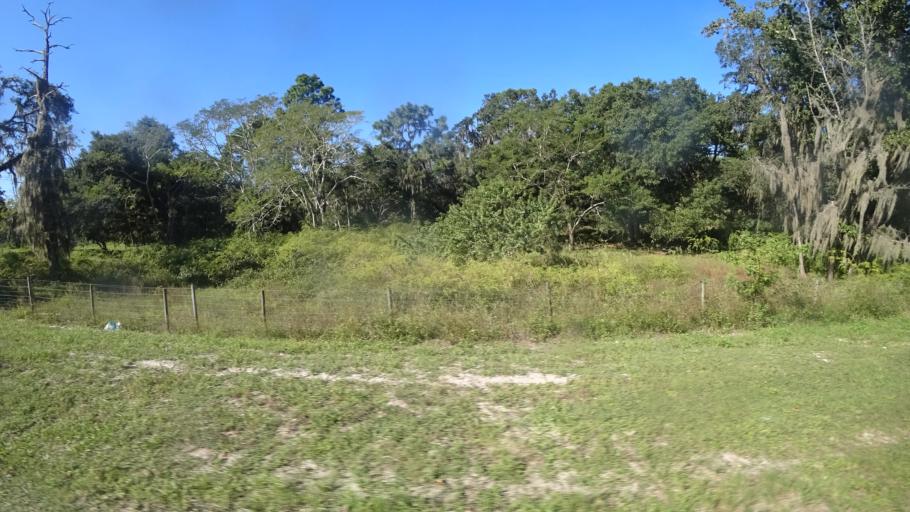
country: US
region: Florida
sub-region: Hillsborough County
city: Wimauma
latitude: 27.6441
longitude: -82.2926
